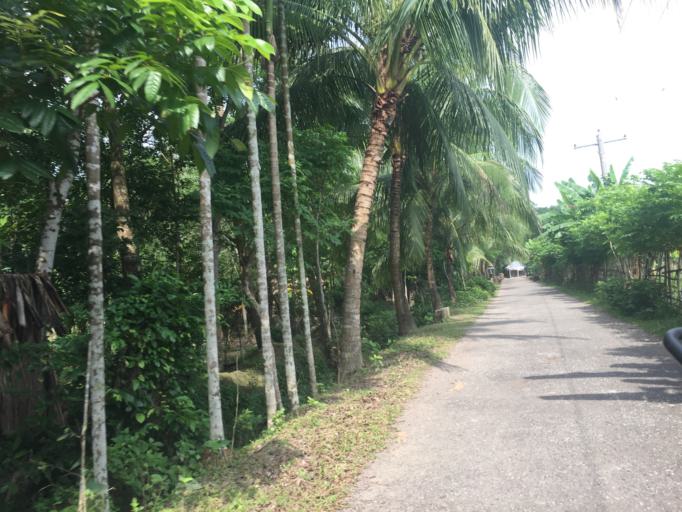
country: BD
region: Barisal
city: Mathba
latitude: 22.2530
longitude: 89.9135
